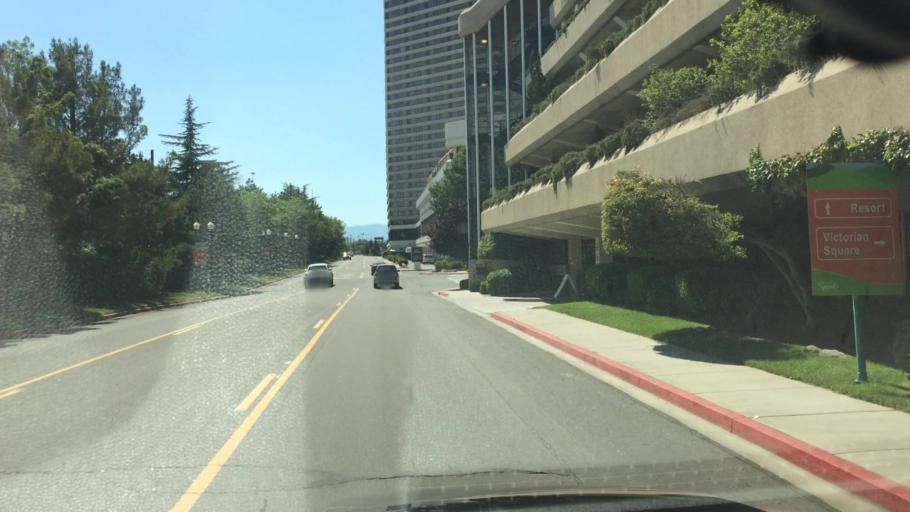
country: US
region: Nevada
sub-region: Washoe County
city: Sparks
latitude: 39.5329
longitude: -119.7563
